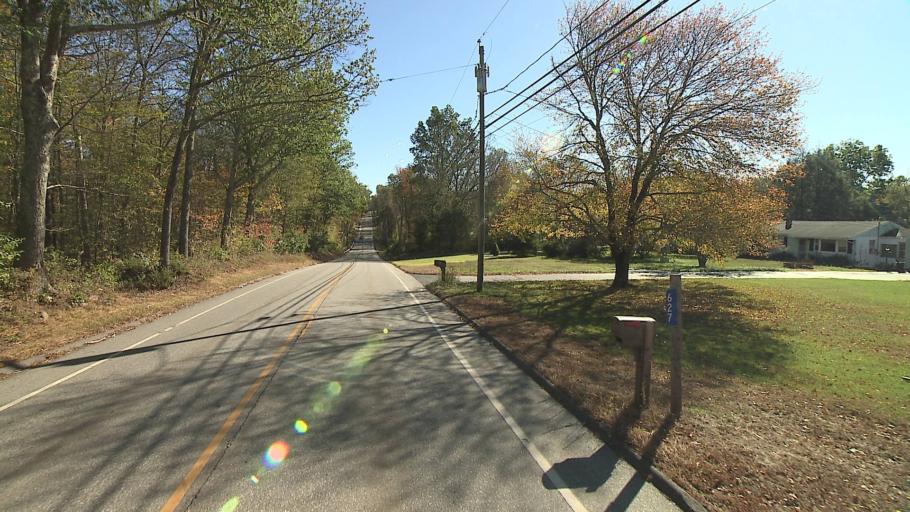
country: US
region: Connecticut
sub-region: Hartford County
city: Terramuggus
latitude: 41.6479
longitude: -72.4190
